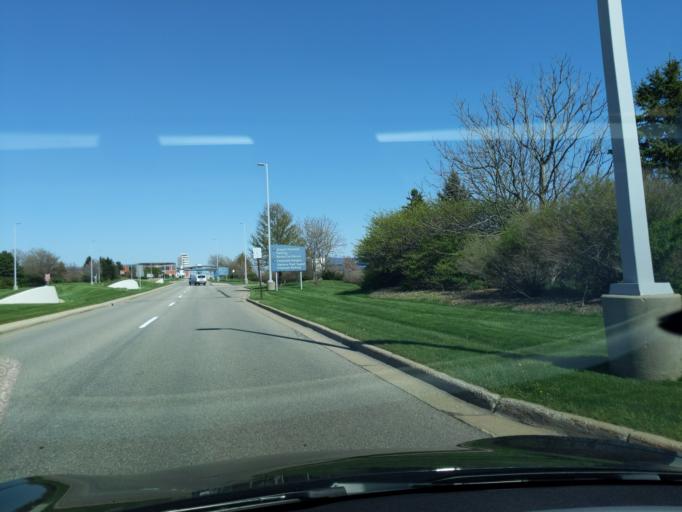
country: US
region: Michigan
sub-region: Kent County
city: Forest Hills
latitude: 42.8836
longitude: -85.5394
